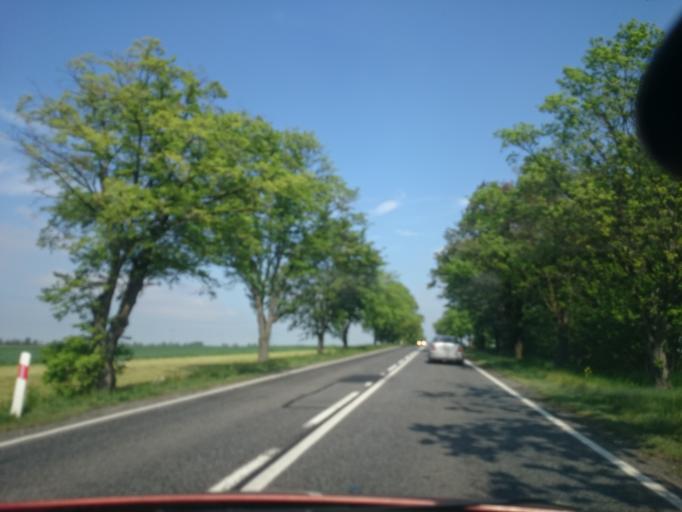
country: PL
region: Opole Voivodeship
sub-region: Powiat opolski
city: Dabrowa
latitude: 50.7100
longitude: 17.7774
